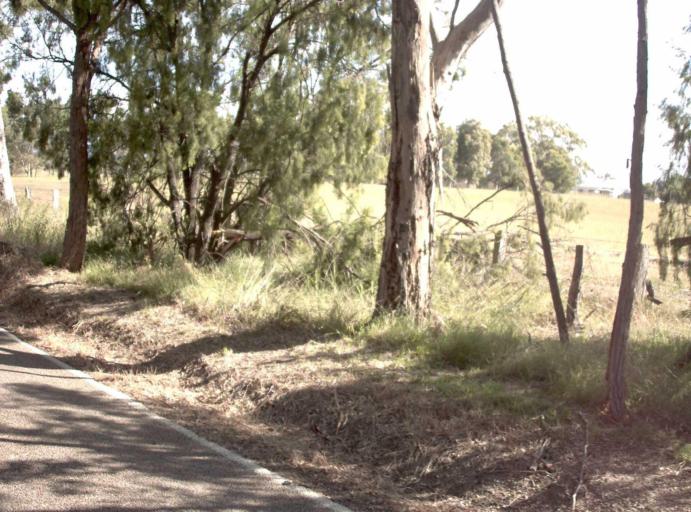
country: AU
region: Victoria
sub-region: East Gippsland
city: Lakes Entrance
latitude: -37.7800
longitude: 147.8241
